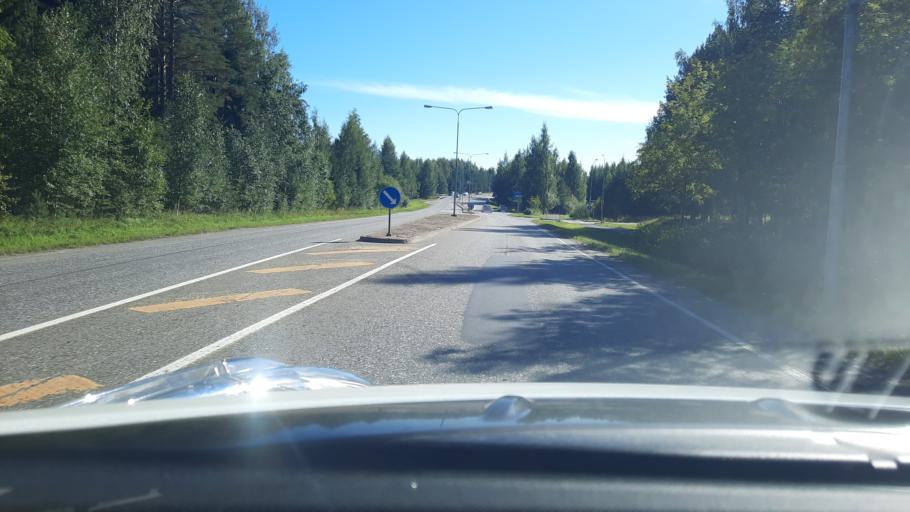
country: FI
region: North Karelia
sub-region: Joensuu
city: Joensuu
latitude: 62.6331
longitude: 29.7005
